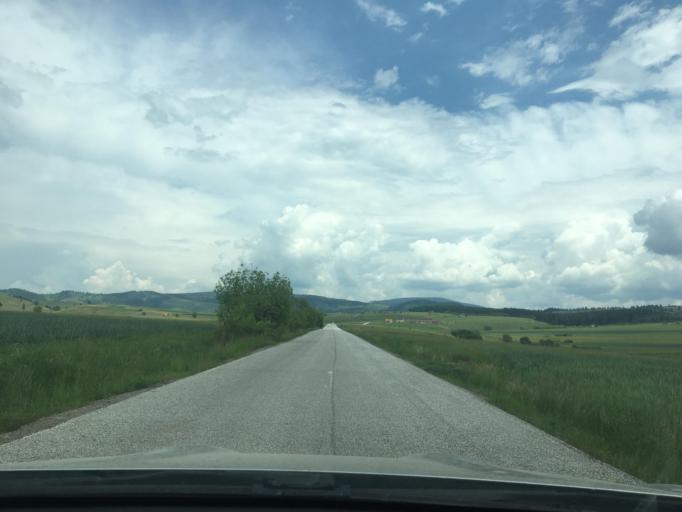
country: RO
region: Harghita
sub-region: Comuna Ditrau
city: Ditrau
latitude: 46.8362
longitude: 25.4947
